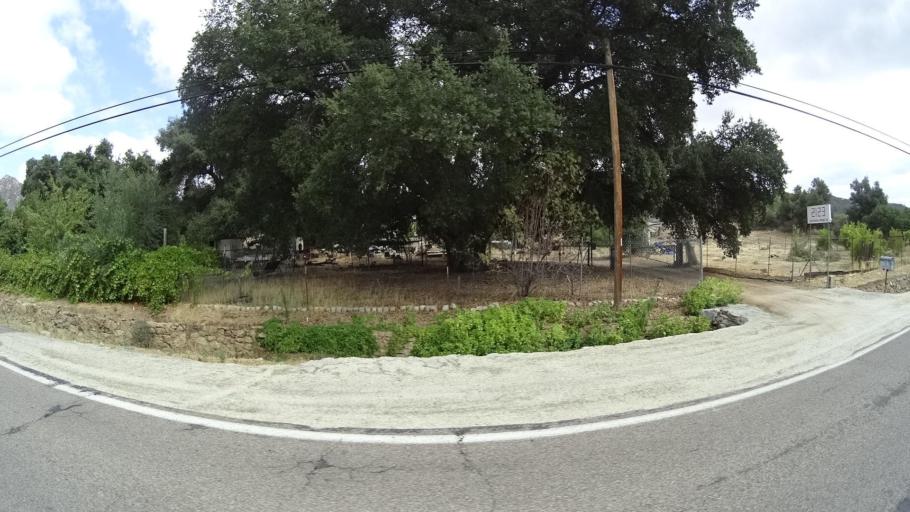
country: US
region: California
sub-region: San Diego County
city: Campo
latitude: 32.6668
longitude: -116.4882
